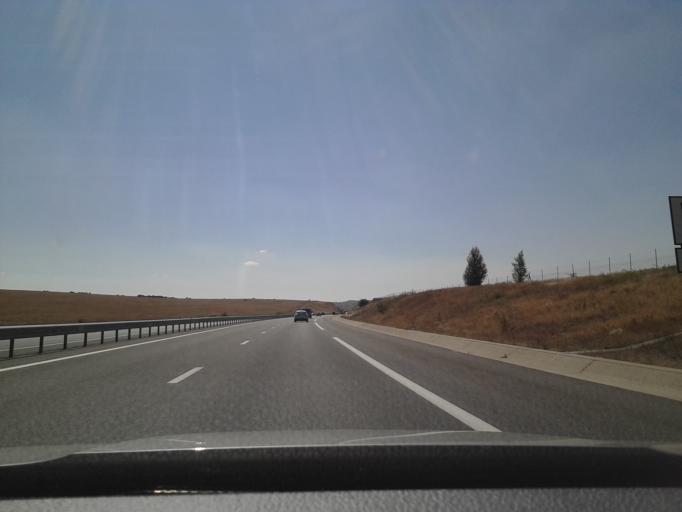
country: FR
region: Midi-Pyrenees
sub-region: Departement de l'Aveyron
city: La Cavalerie
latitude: 44.0258
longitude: 3.1147
